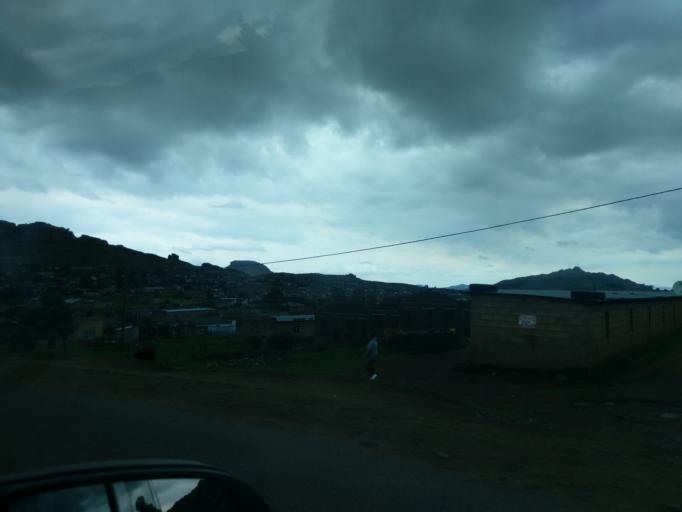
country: LS
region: Mohale's Hoek District
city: Mohale's Hoek
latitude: -30.1322
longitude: 27.4673
